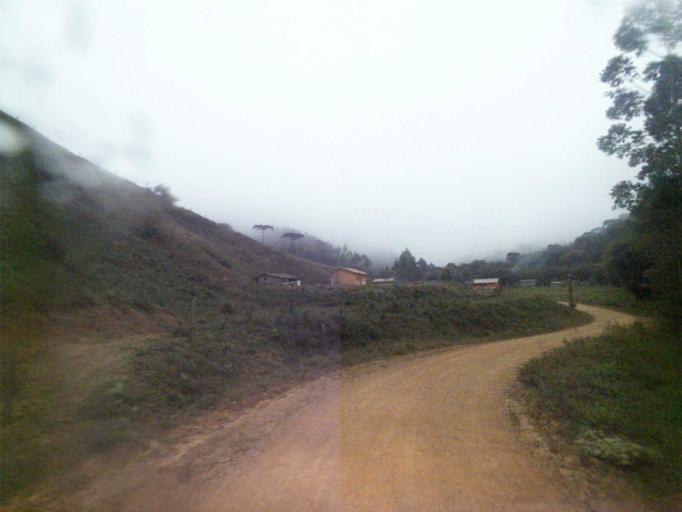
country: BR
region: Santa Catarina
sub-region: Anitapolis
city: Anitapolis
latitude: -27.8057
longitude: -49.1411
